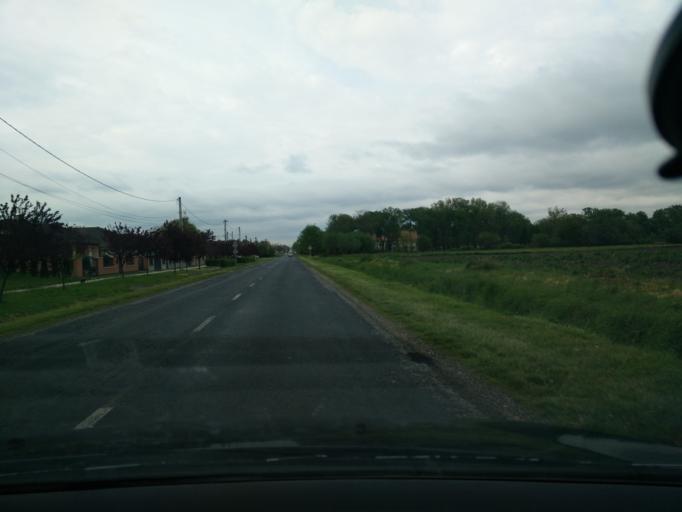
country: HU
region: Veszprem
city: Papa
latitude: 47.2802
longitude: 17.4181
